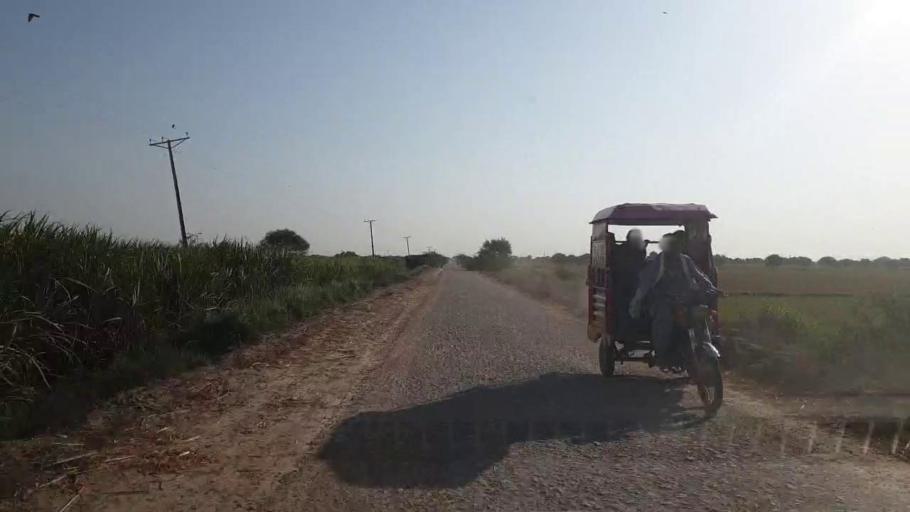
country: PK
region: Sindh
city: Talhar
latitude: 24.9385
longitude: 68.7513
